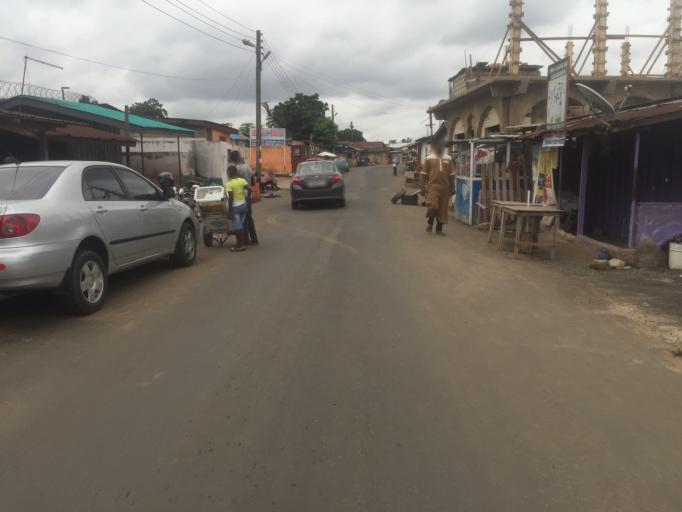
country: GH
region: Greater Accra
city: Dome
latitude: 5.6020
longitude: -0.2250
